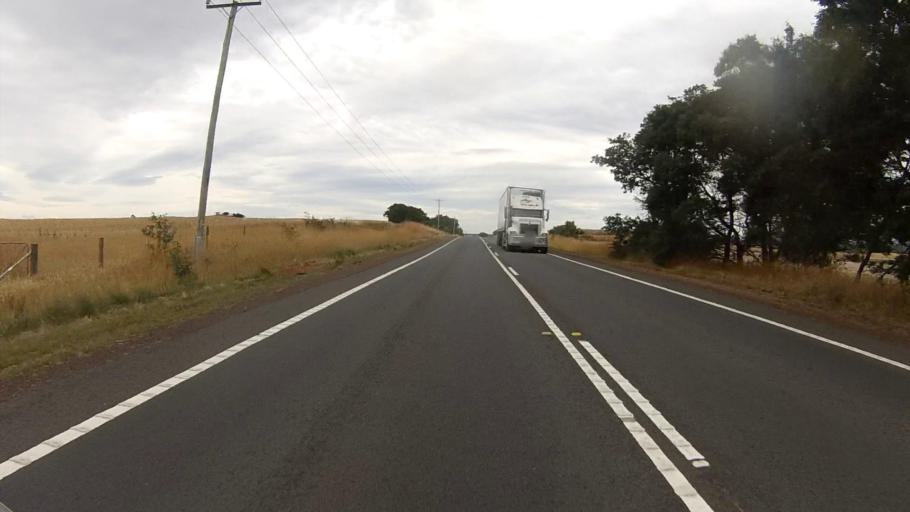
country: AU
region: Tasmania
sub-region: Northern Midlands
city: Evandale
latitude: -41.9074
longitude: 147.4797
